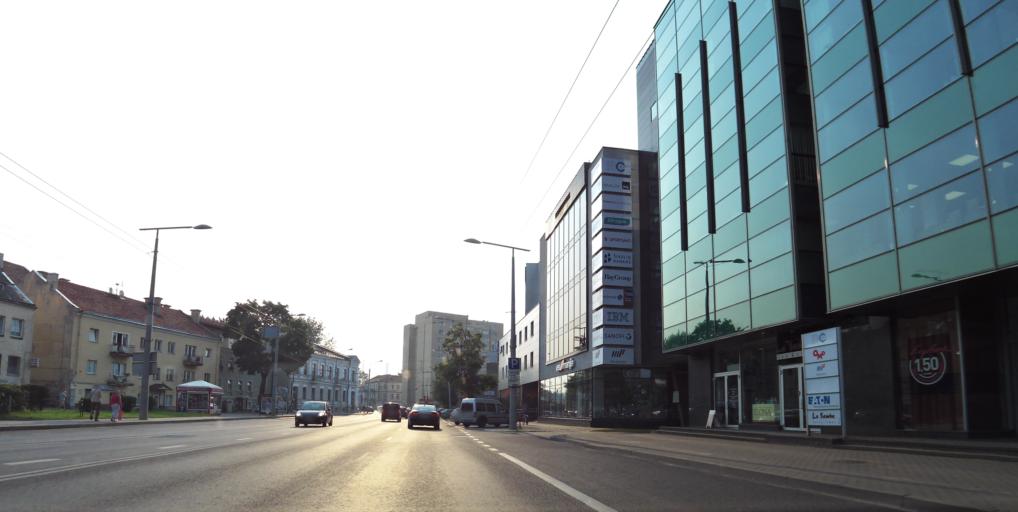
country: LT
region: Vilnius County
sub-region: Vilnius
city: Vilnius
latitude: 54.6945
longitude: 25.2828
